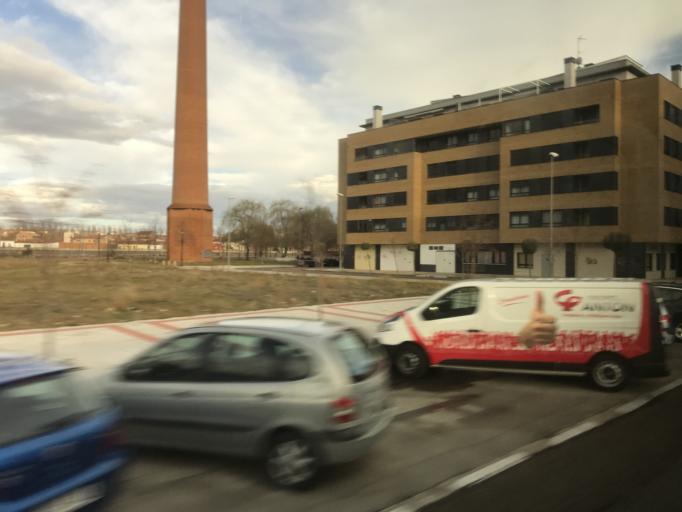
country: ES
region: Castille and Leon
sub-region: Provincia de Palencia
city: Palencia
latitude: 42.0210
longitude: -4.5442
